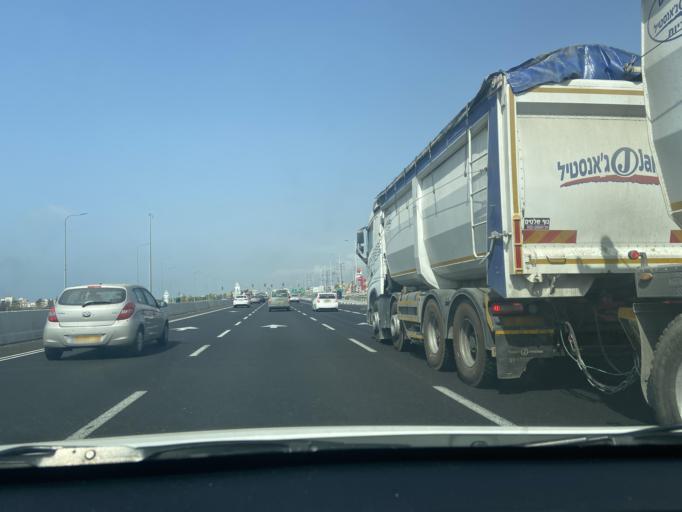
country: IL
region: Northern District
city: El Mazra`a
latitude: 32.9762
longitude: 35.0934
